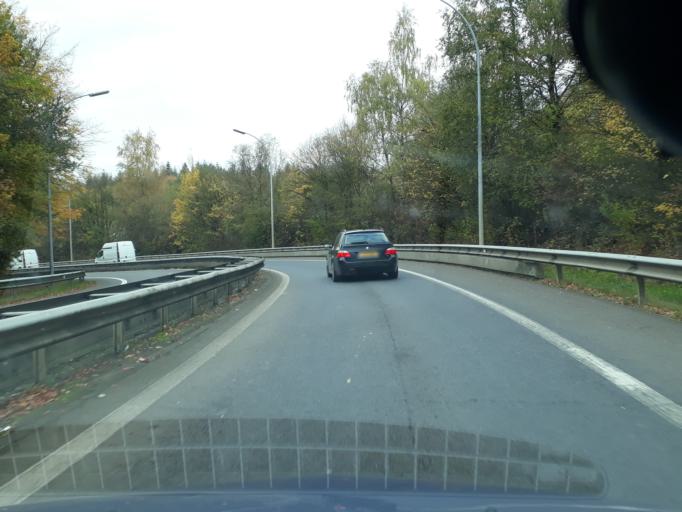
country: LU
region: Luxembourg
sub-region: Canton de Luxembourg
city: Sandweiler
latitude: 49.6436
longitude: 6.2181
